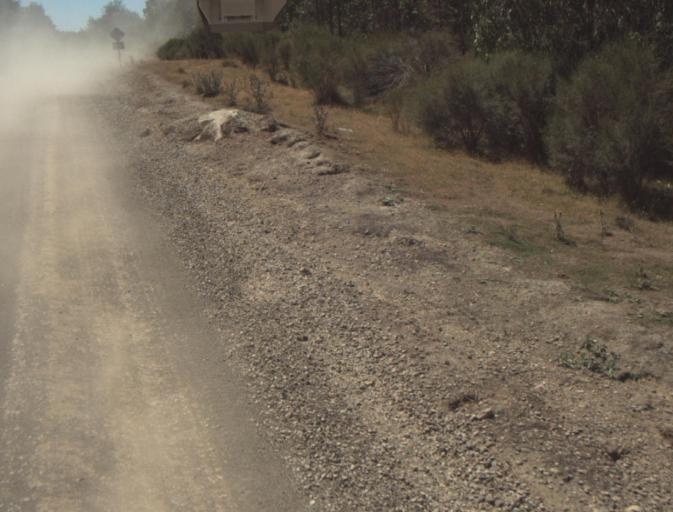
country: AU
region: Tasmania
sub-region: Dorset
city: Scottsdale
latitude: -41.3121
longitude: 147.4660
